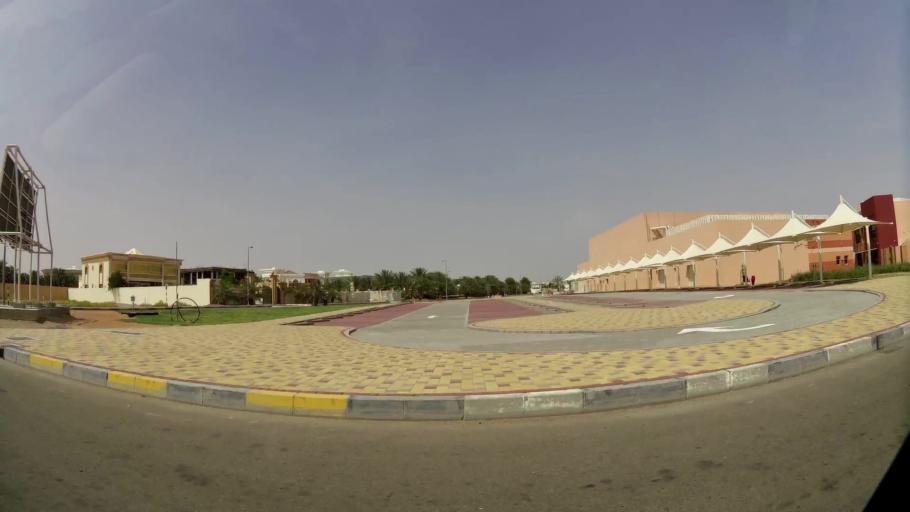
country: AE
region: Abu Dhabi
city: Al Ain
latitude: 24.1604
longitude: 55.6620
